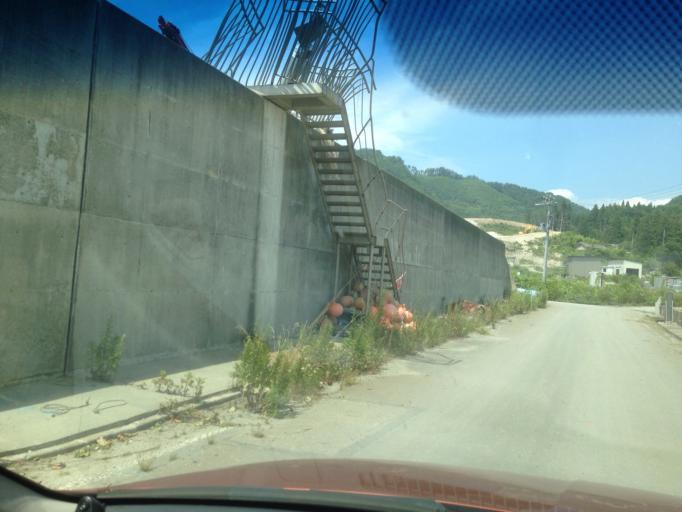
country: JP
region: Iwate
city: Otsuchi
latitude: 39.3515
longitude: 141.9339
